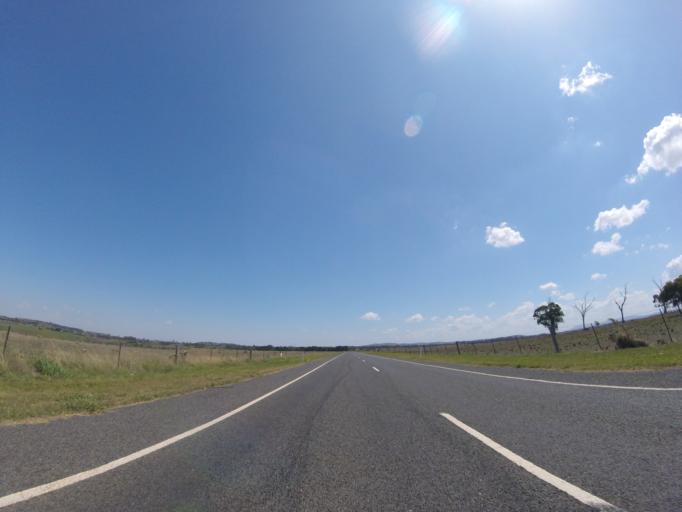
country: AU
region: Victoria
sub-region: Hume
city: Sunbury
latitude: -37.5856
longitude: 144.7809
